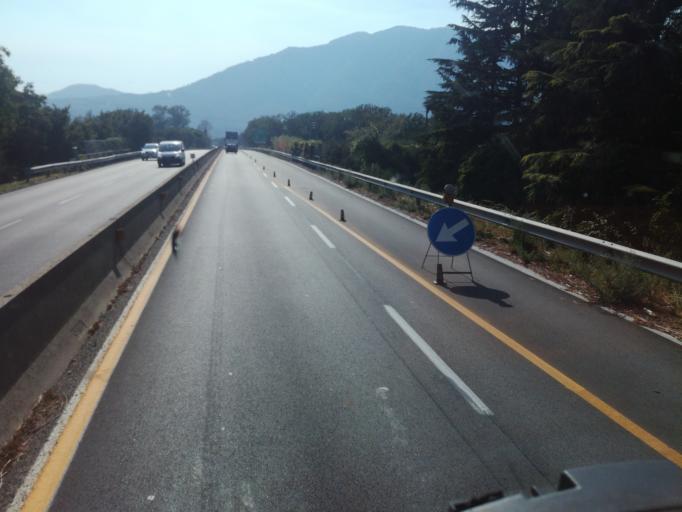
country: IT
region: Campania
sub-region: Provincia di Avellino
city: San Pietro
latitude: 40.8173
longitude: 14.7875
